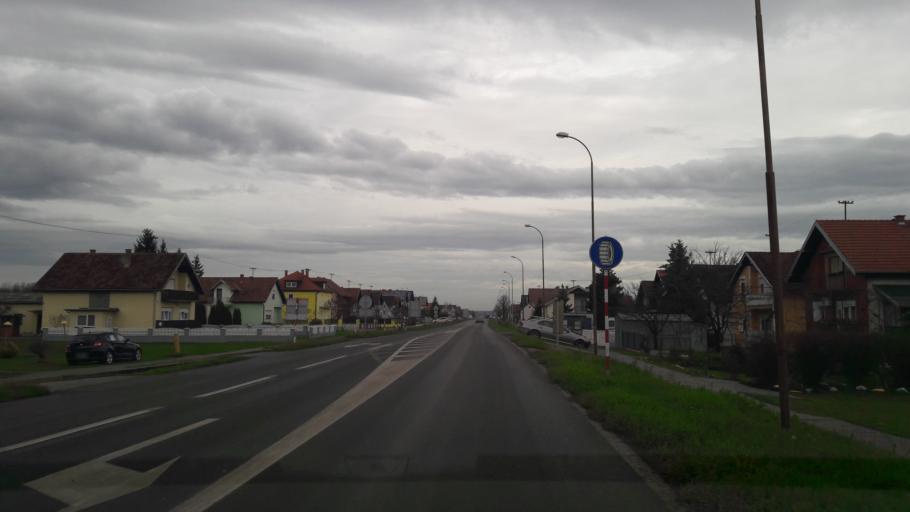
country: HR
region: Osjecko-Baranjska
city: Velimirovac
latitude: 45.5139
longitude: 18.0951
